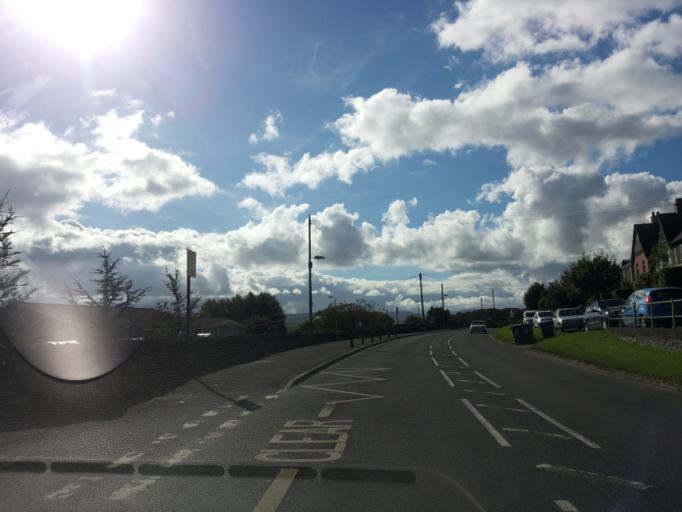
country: GB
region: England
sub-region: North Yorkshire
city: Leyburn
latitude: 54.3143
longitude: -1.8239
